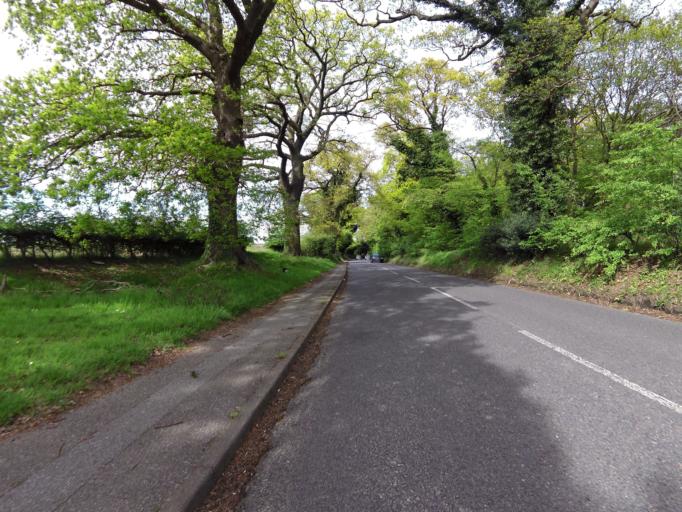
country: GB
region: England
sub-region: Essex
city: Mistley
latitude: 51.9754
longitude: 1.1530
